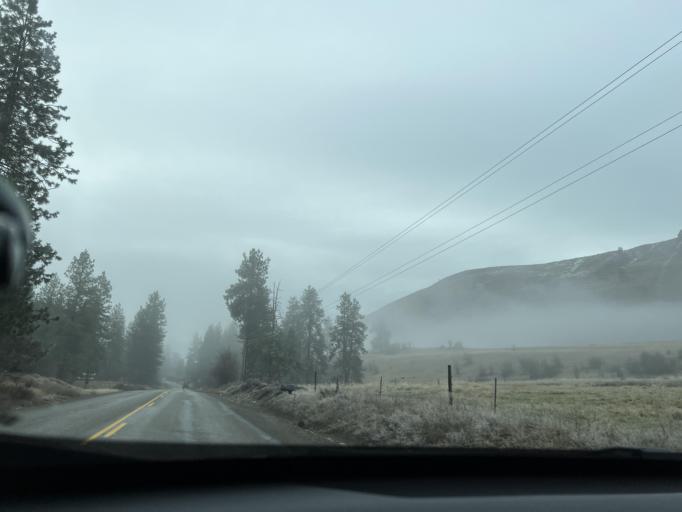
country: US
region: Washington
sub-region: Okanogan County
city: Brewster
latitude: 48.4570
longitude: -120.2059
